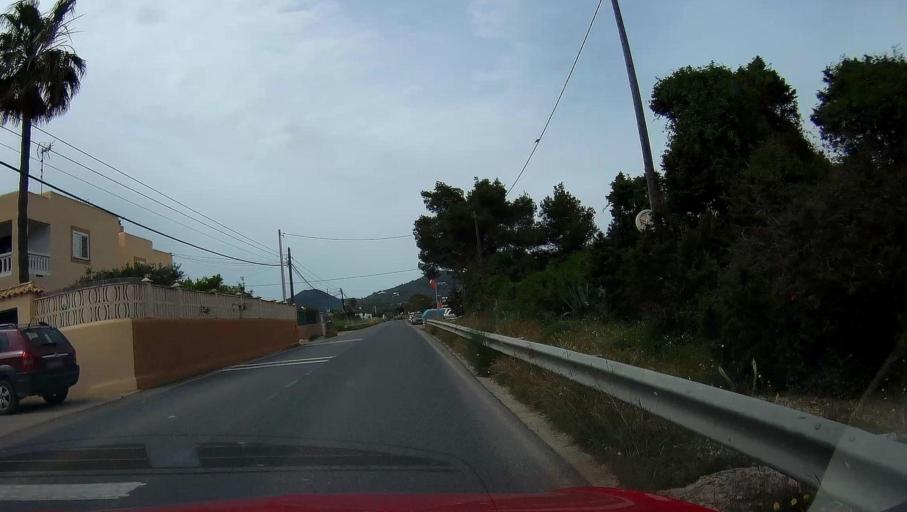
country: ES
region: Balearic Islands
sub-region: Illes Balears
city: Ibiza
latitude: 38.8773
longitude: 1.3644
